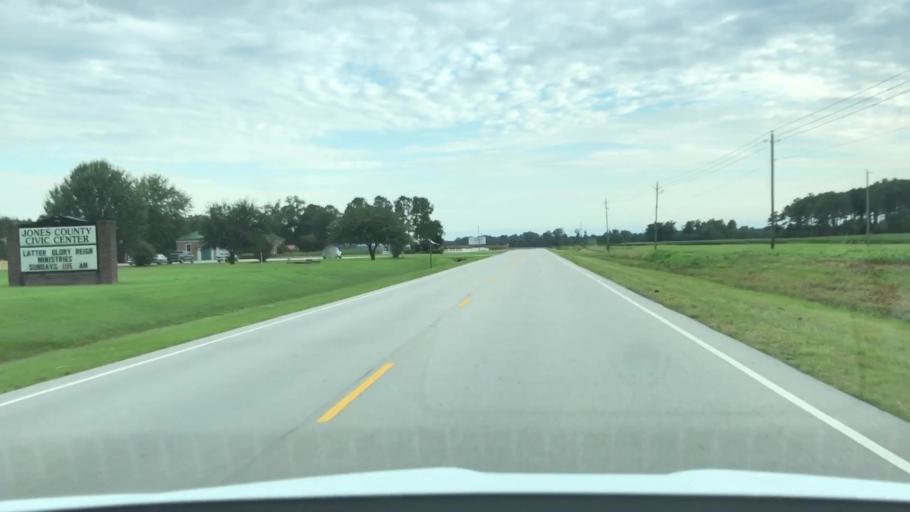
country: US
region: North Carolina
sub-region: Jones County
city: Trenton
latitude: 35.0440
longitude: -77.3511
